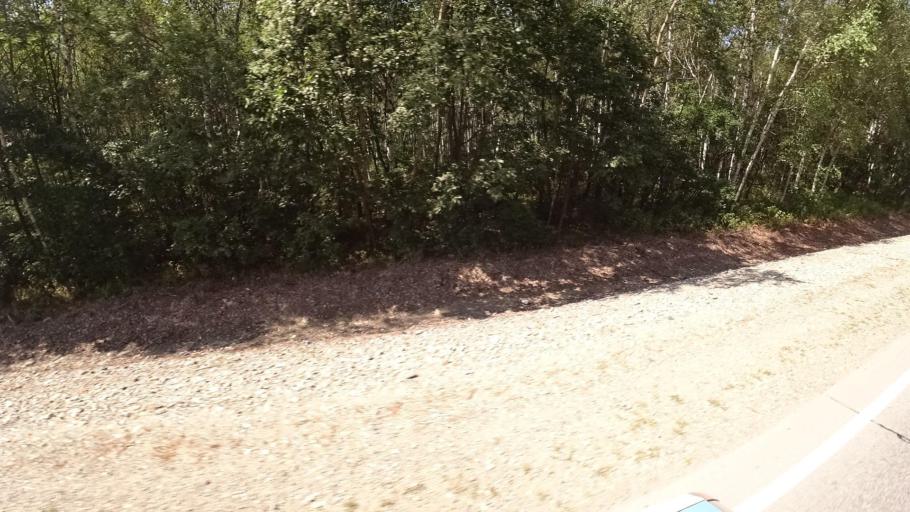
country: RU
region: Khabarovsk Krai
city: Khor
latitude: 47.9813
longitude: 135.0868
